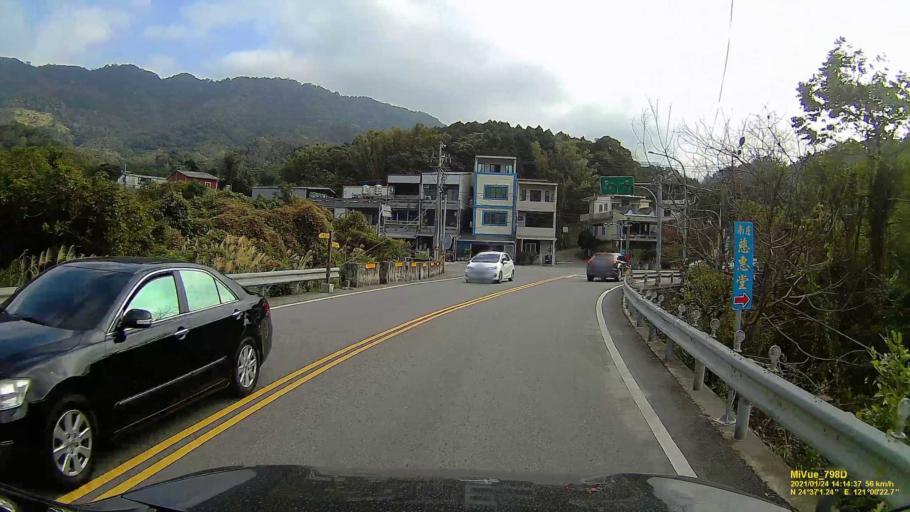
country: TW
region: Taiwan
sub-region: Miaoli
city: Miaoli
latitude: 24.6167
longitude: 121.0064
